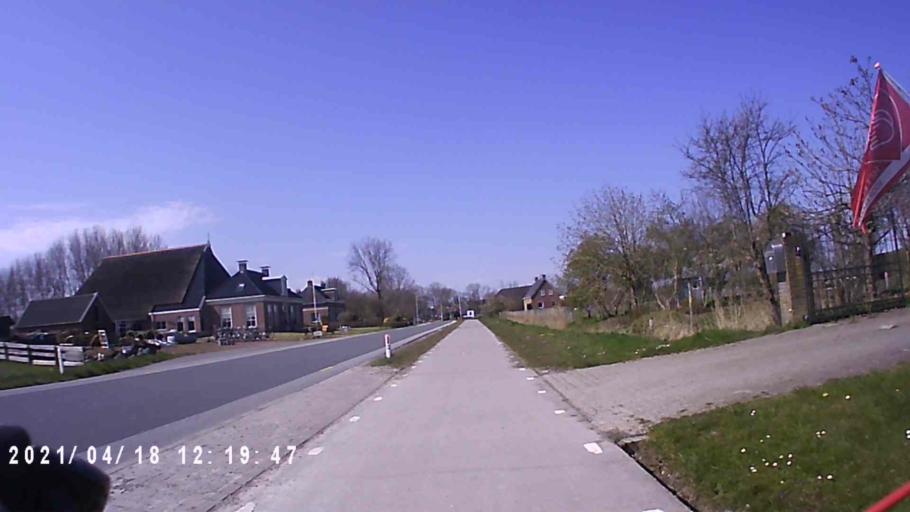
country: NL
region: Friesland
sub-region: Gemeente Kollumerland en Nieuwkruisland
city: Kollum
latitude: 53.3225
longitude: 6.1436
